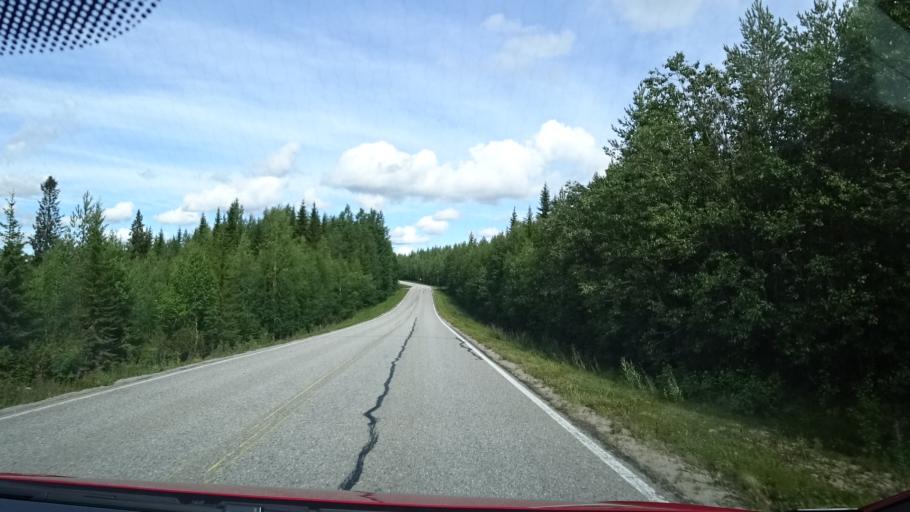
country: FI
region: Kainuu
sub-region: Kehys-Kainuu
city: Kuhmo
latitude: 64.4305
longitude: 29.8117
